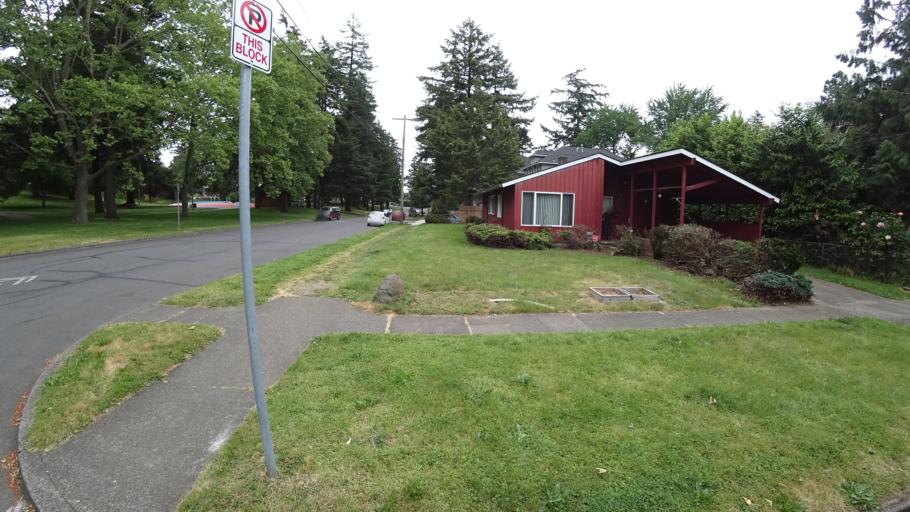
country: US
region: Oregon
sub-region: Multnomah County
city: Lents
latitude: 45.4846
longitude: -122.5709
